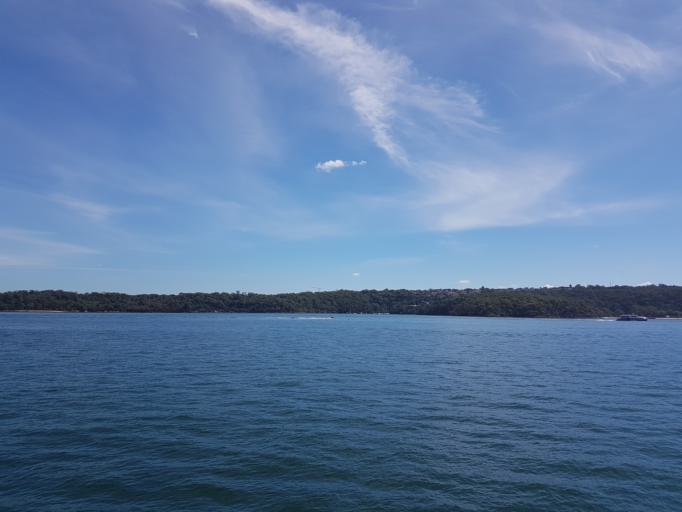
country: AU
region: New South Wales
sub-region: Woollahra
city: Point Piper
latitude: -33.8510
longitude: 151.2623
